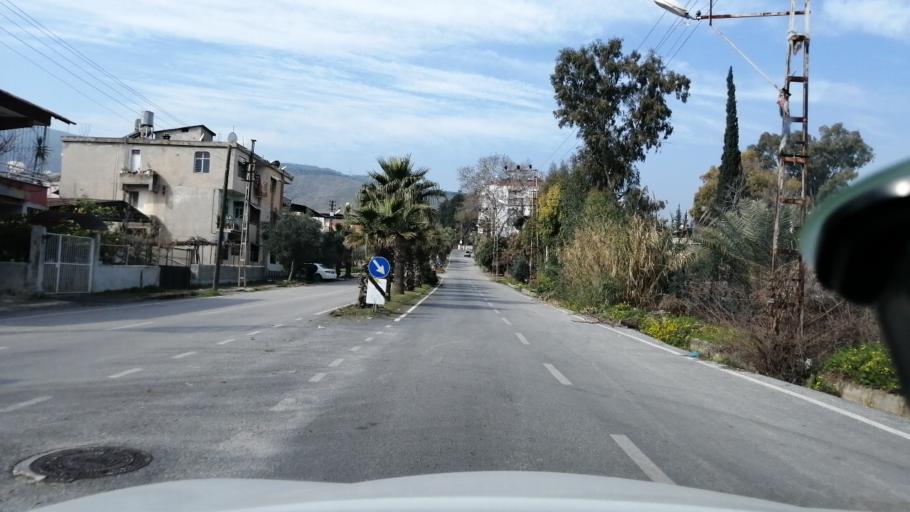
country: TR
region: Hatay
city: Serinyol
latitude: 36.3530
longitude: 36.2094
